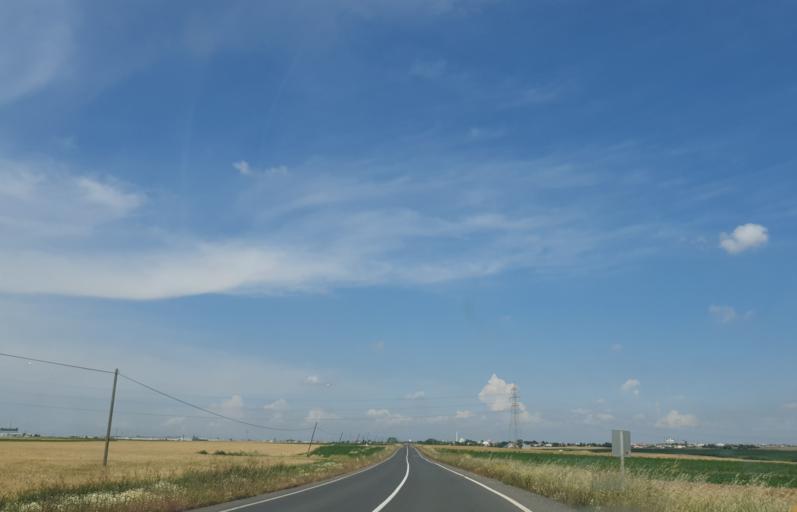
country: TR
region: Kirklareli
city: Buyukkaristiran
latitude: 41.2508
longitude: 27.6199
